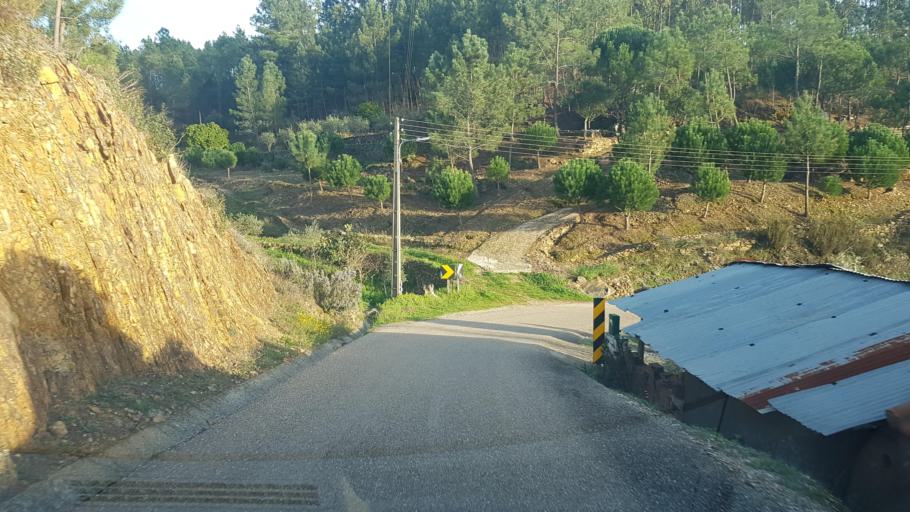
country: PT
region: Castelo Branco
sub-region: Vila de Rei
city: Vila de Rei
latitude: 39.6003
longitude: -8.1209
